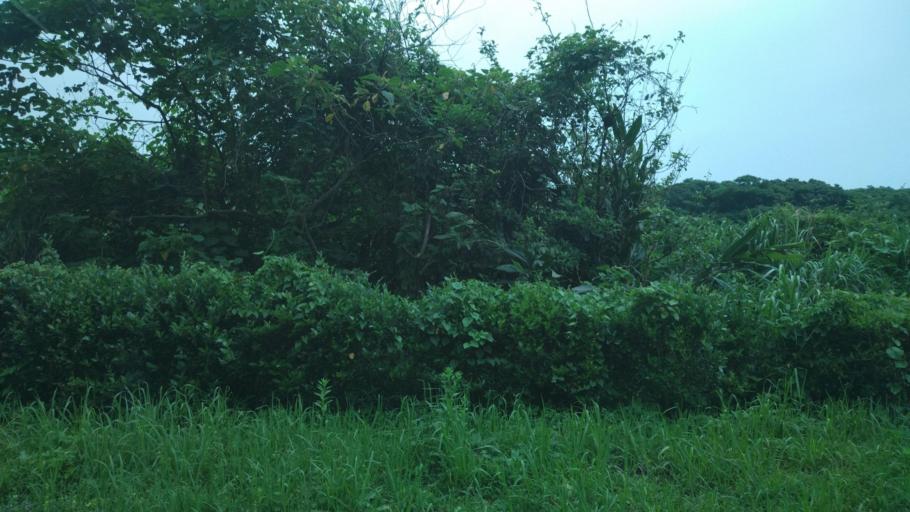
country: TW
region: Taiwan
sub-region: Keelung
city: Keelung
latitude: 25.2090
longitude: 121.6526
